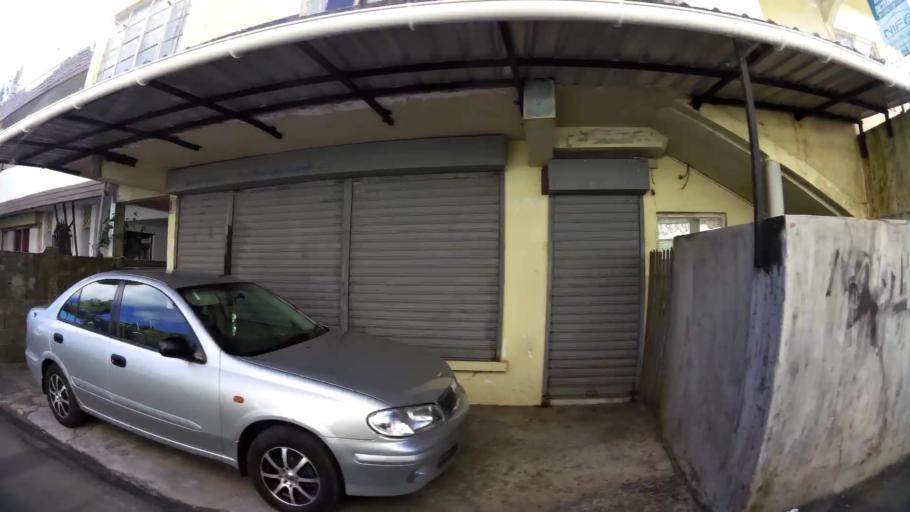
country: MU
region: Plaines Wilhems
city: Curepipe
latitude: -20.2906
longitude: 57.5155
